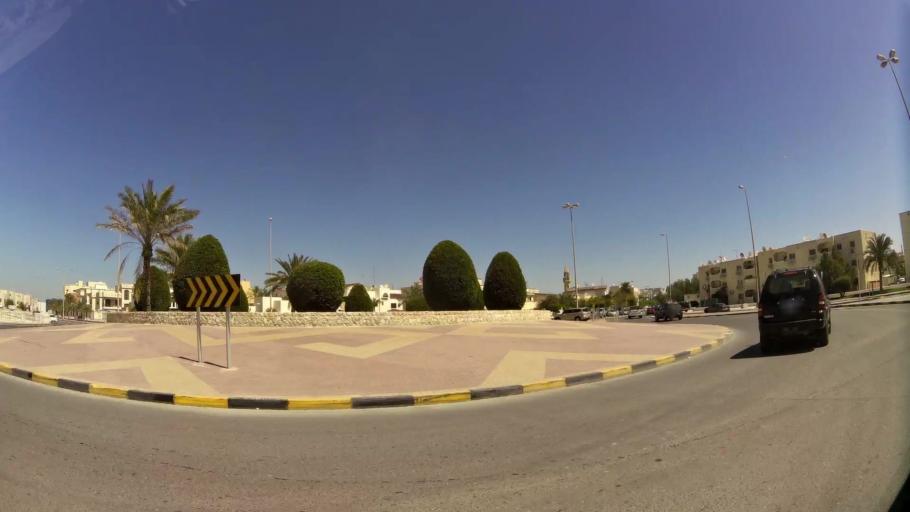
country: BH
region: Muharraq
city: Al Muharraq
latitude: 26.2665
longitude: 50.6030
